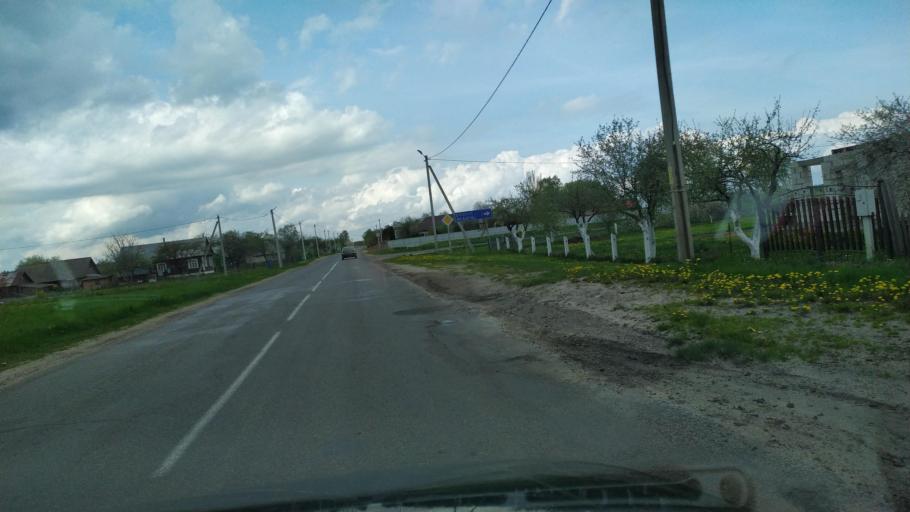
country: BY
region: Brest
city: Pruzhany
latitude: 52.5876
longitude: 24.4105
